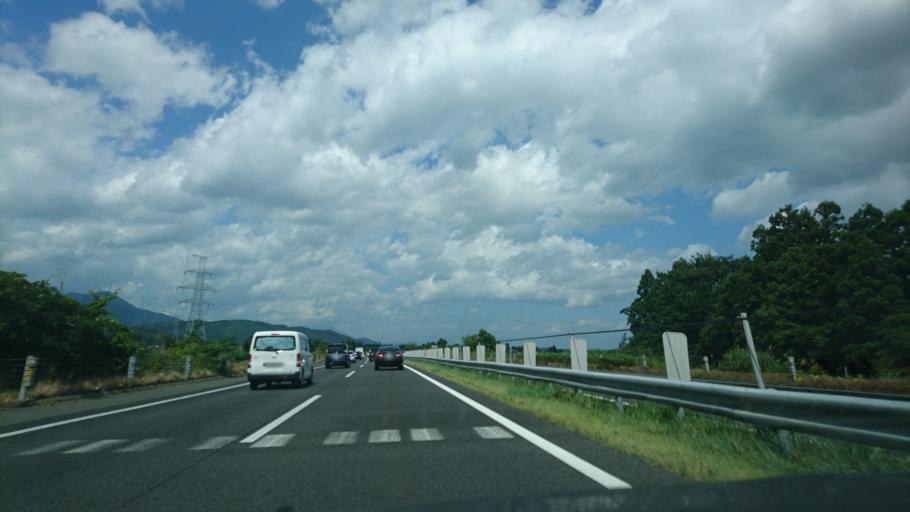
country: JP
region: Iwate
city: Morioka-shi
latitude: 39.5788
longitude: 141.1200
